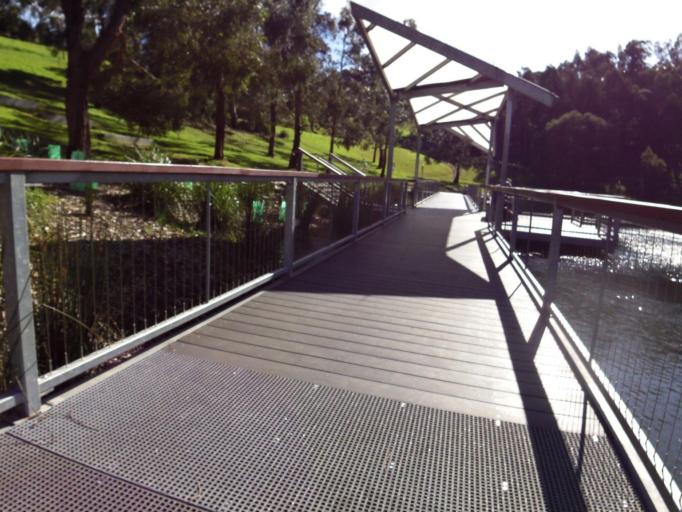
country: AU
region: Victoria
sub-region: Knox
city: Ferntree Gully
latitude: -37.8884
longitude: 145.3013
